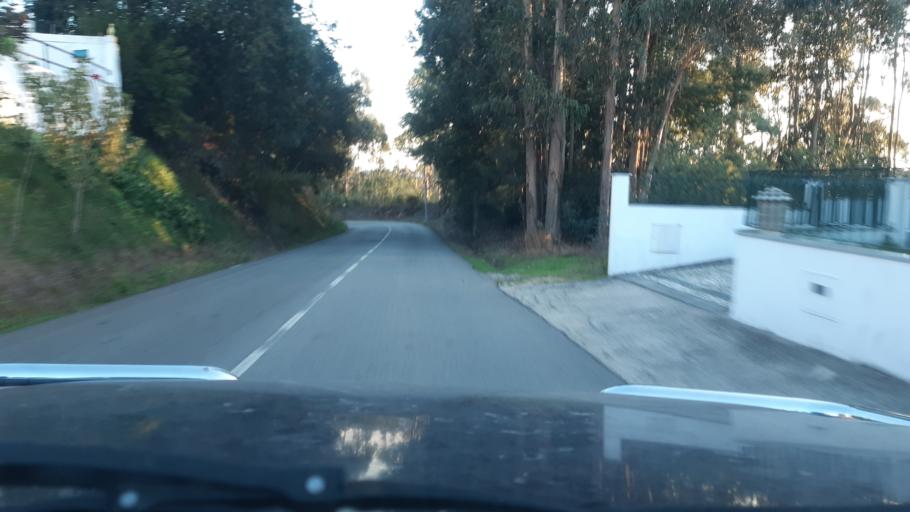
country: PT
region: Aveiro
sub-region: Agueda
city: Agueda
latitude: 40.5792
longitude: -8.4632
